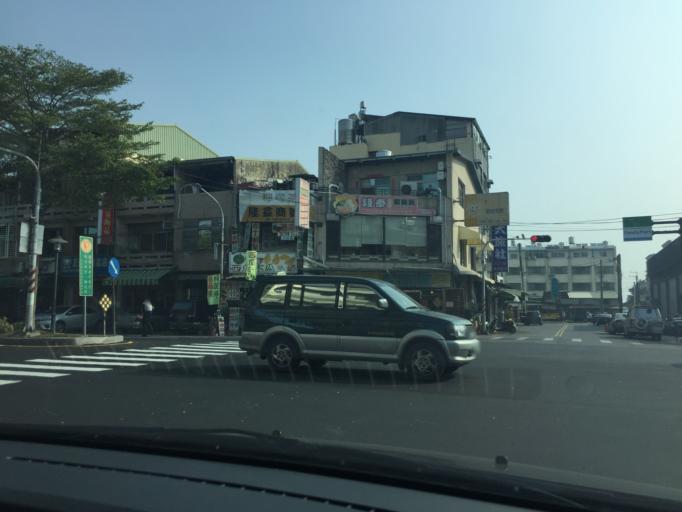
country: TW
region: Taiwan
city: Xinying
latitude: 23.1928
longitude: 120.3183
